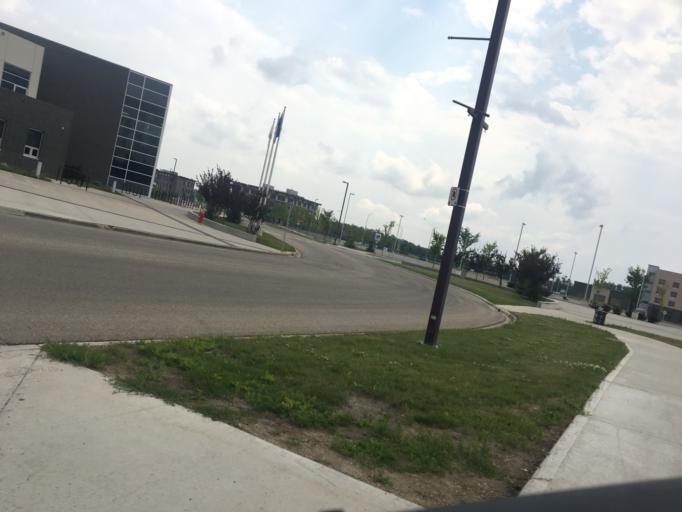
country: CA
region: Alberta
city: Grande Prairie
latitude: 55.1433
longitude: -118.8158
